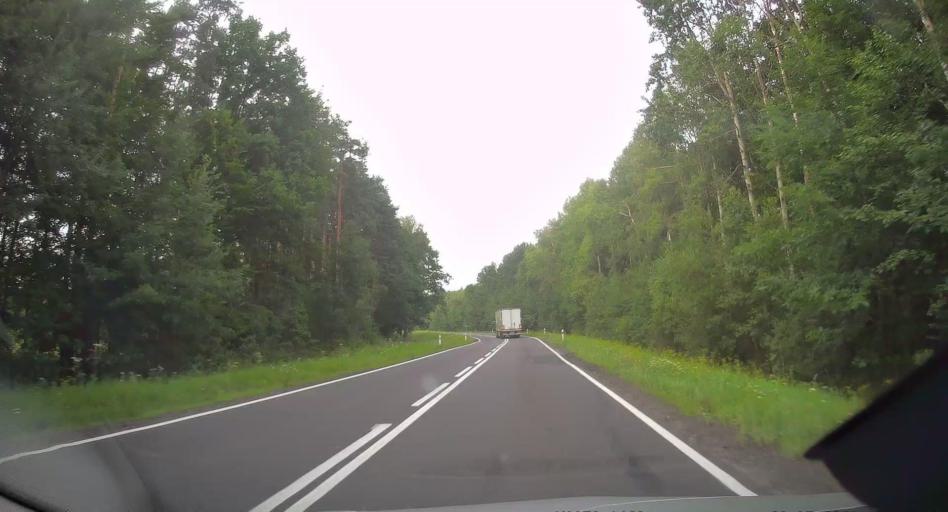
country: PL
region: Silesian Voivodeship
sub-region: Powiat czestochowski
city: Klomnice
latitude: 50.9549
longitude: 19.4021
